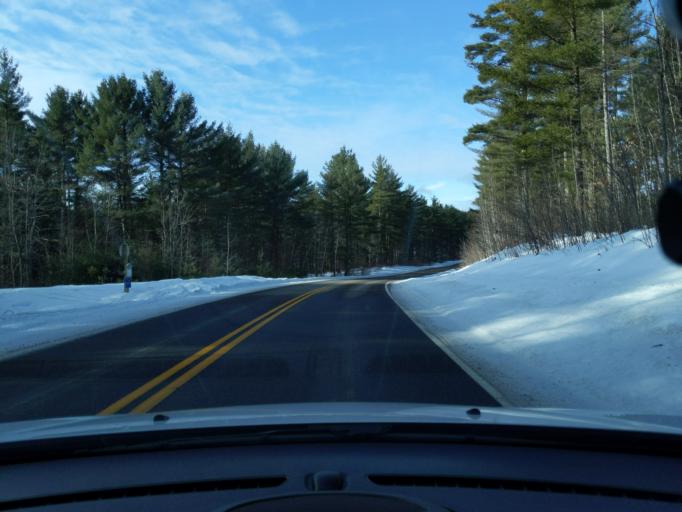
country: US
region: Wisconsin
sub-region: Sawyer County
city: Little Round Lake
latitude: 46.1114
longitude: -91.3111
